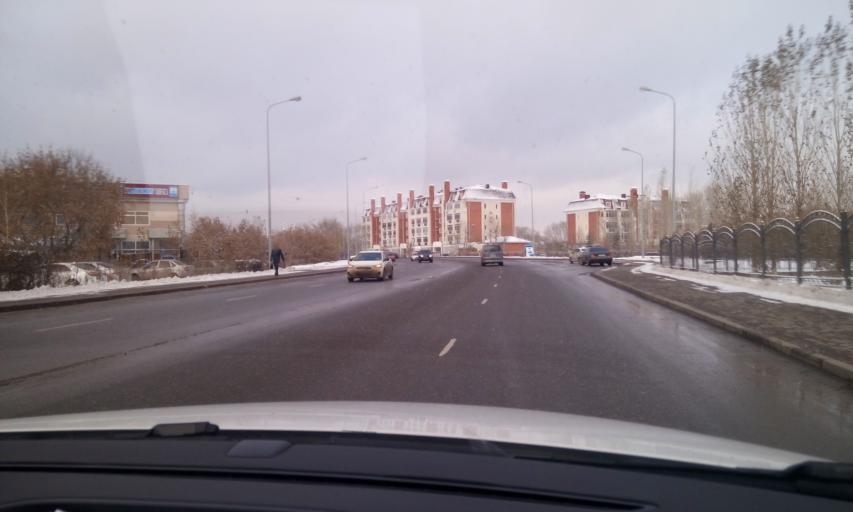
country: KZ
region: Astana Qalasy
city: Astana
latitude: 51.1350
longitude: 71.4353
